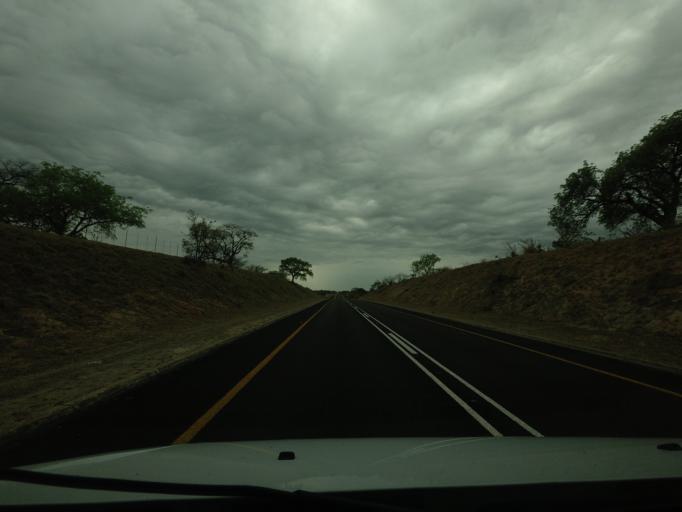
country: ZA
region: Limpopo
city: Thulamahashi
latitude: -24.5679
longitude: 31.0839
